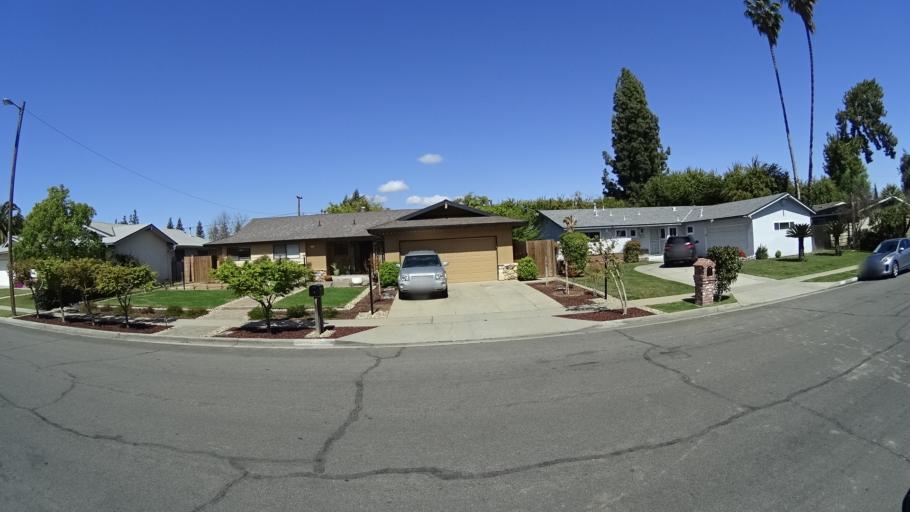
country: US
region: California
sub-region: Fresno County
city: Fresno
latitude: 36.8259
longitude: -119.8024
